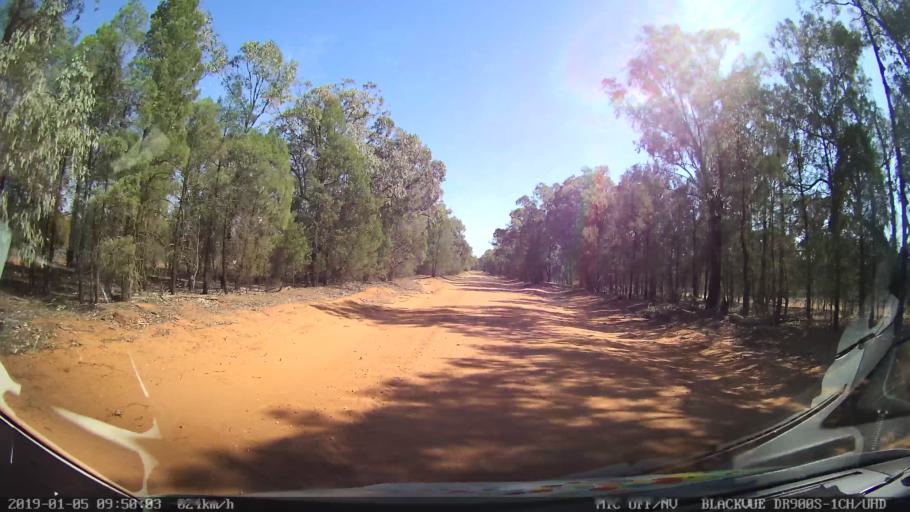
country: AU
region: New South Wales
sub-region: Gilgandra
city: Gilgandra
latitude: -31.6661
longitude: 148.7586
